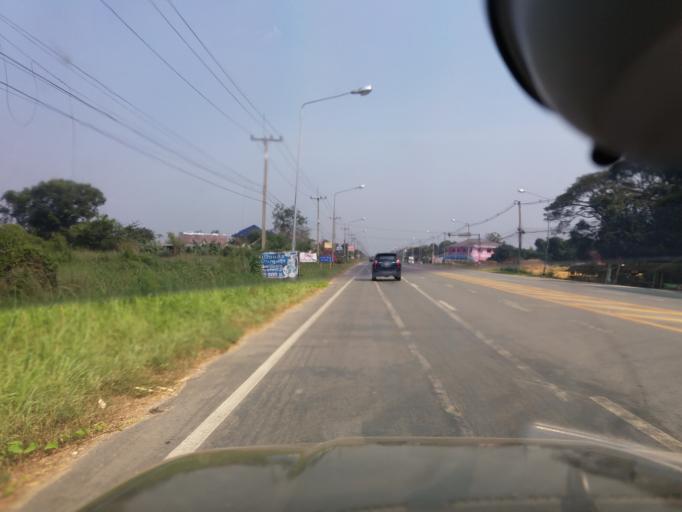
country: TH
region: Sing Buri
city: Bang Racham
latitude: 14.8826
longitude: 100.3287
